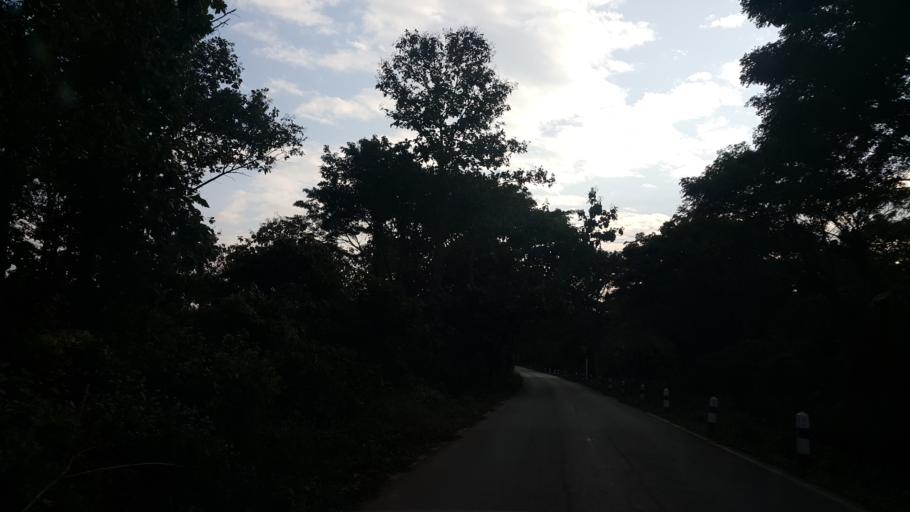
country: TH
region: Lampang
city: Sop Prap
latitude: 17.9222
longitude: 99.3289
